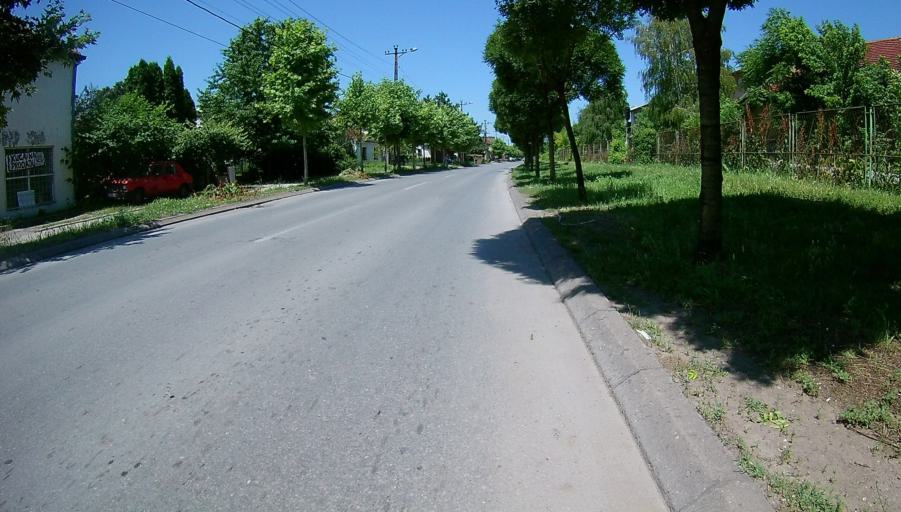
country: RS
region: Central Serbia
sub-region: Nisavski Okrug
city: Nis
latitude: 43.3133
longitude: 21.8876
